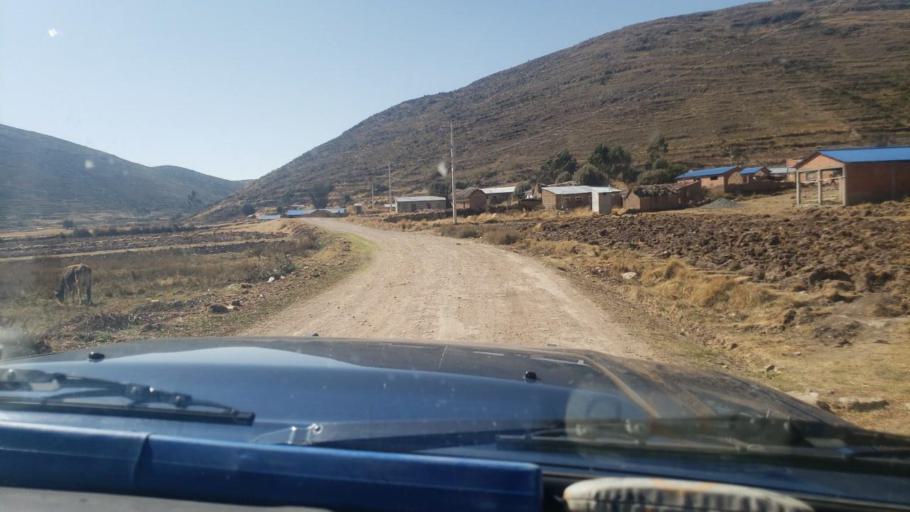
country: BO
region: La Paz
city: Huatajata
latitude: -16.3403
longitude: -68.6766
